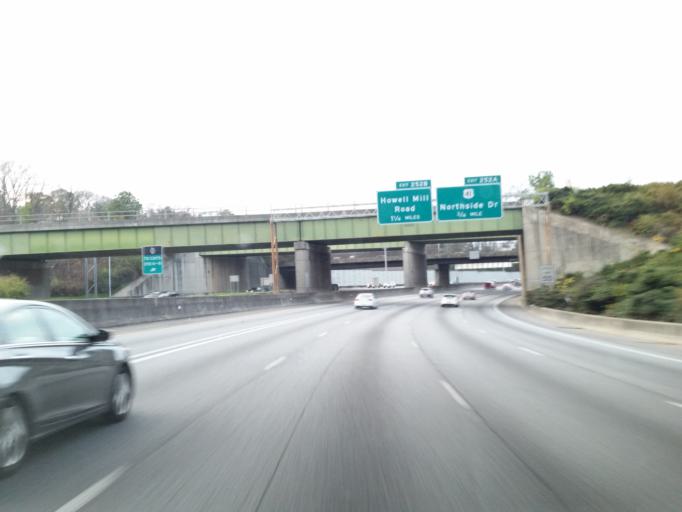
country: US
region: Georgia
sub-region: Fulton County
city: Atlanta
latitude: 33.7964
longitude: -84.3938
